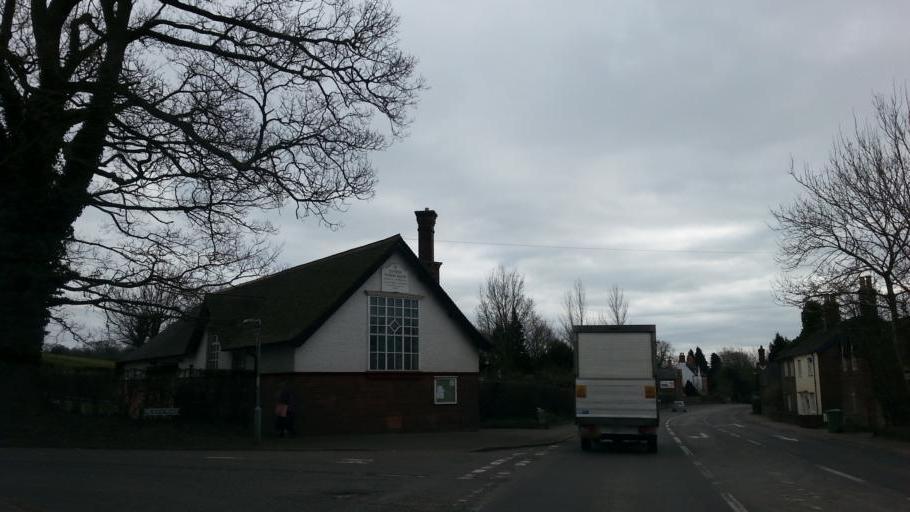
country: GB
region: England
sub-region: Staffordshire
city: Stafford
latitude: 52.8649
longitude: -2.0796
